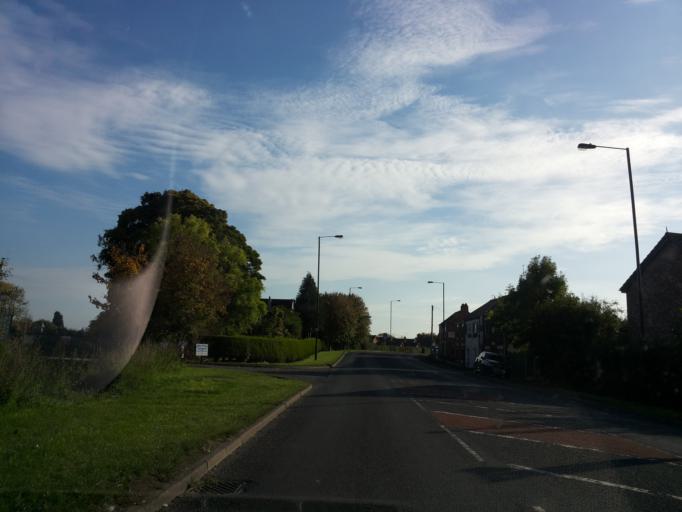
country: GB
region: England
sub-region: Doncaster
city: Hatfield
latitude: 53.6057
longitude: -0.9642
